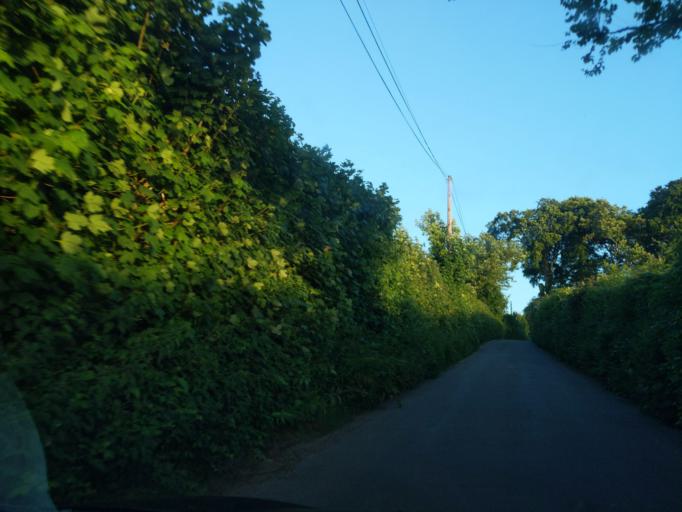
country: GB
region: England
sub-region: Devon
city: Great Torrington
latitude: 50.9415
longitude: -4.1528
